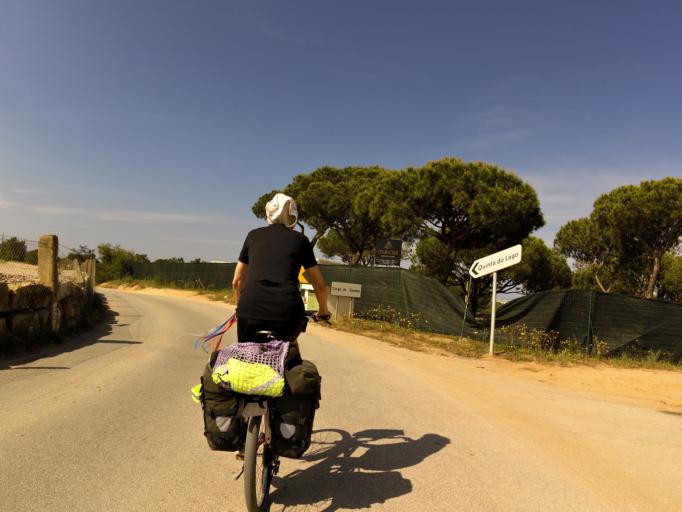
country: PT
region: Faro
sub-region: Loule
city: Almancil
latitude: 37.0664
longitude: -8.0145
